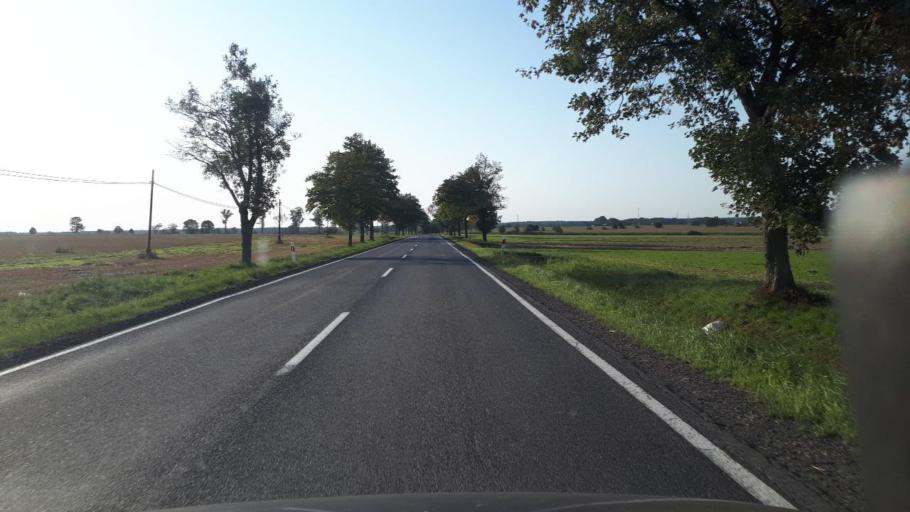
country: PL
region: Silesian Voivodeship
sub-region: Powiat lubliniecki
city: Sierakow Slaski
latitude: 50.8337
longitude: 18.5153
